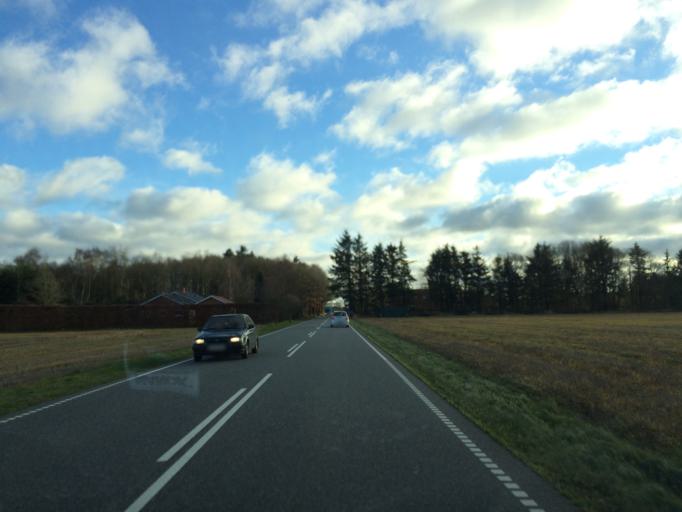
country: DK
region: Central Jutland
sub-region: Herning Kommune
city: Kibaek
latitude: 55.9294
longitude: 8.8993
